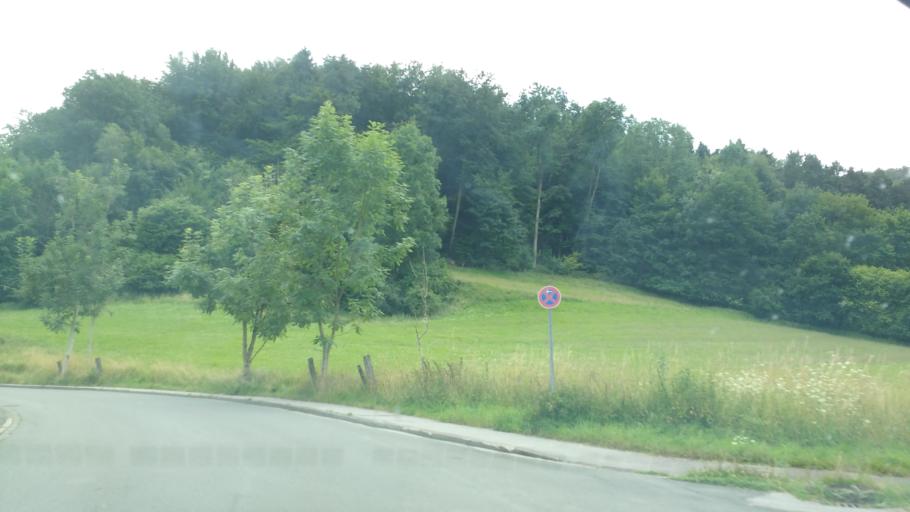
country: DE
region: North Rhine-Westphalia
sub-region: Regierungsbezirk Detmold
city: Detmold
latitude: 51.8883
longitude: 8.8697
